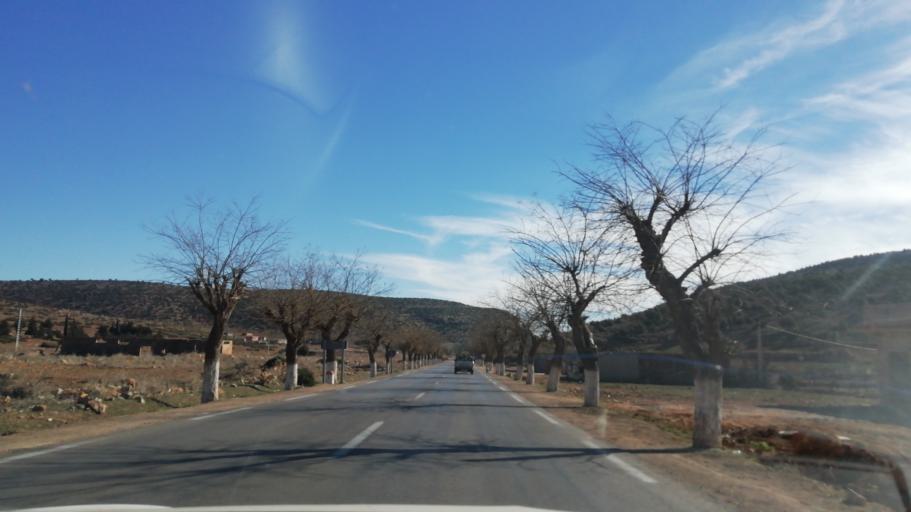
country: DZ
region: Tlemcen
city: Sebdou
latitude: 34.7042
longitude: -1.3173
